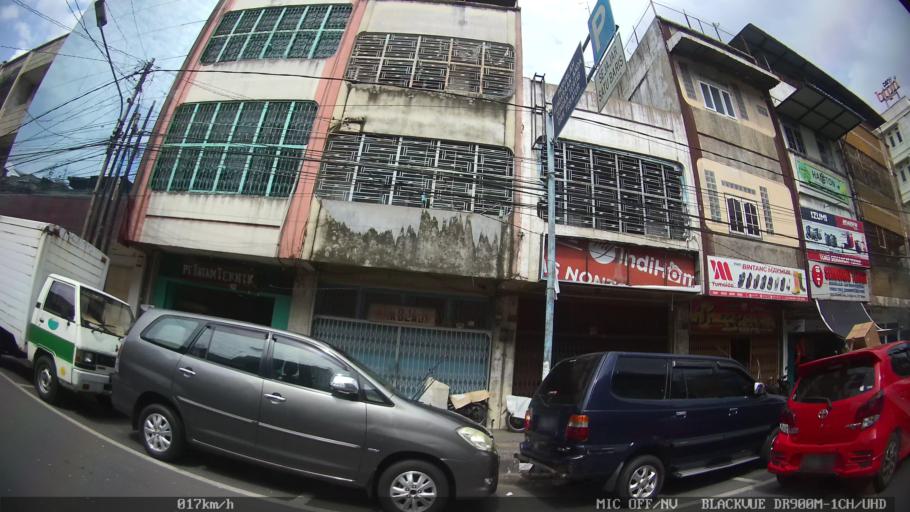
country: ID
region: North Sumatra
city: Medan
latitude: 3.5845
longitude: 98.6839
